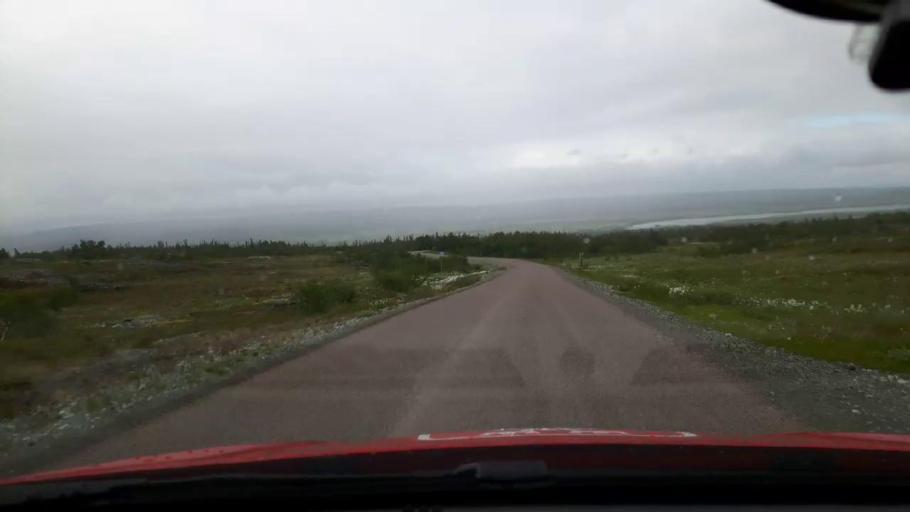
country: SE
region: Jaemtland
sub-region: Are Kommun
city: Are
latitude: 63.2444
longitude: 12.4304
